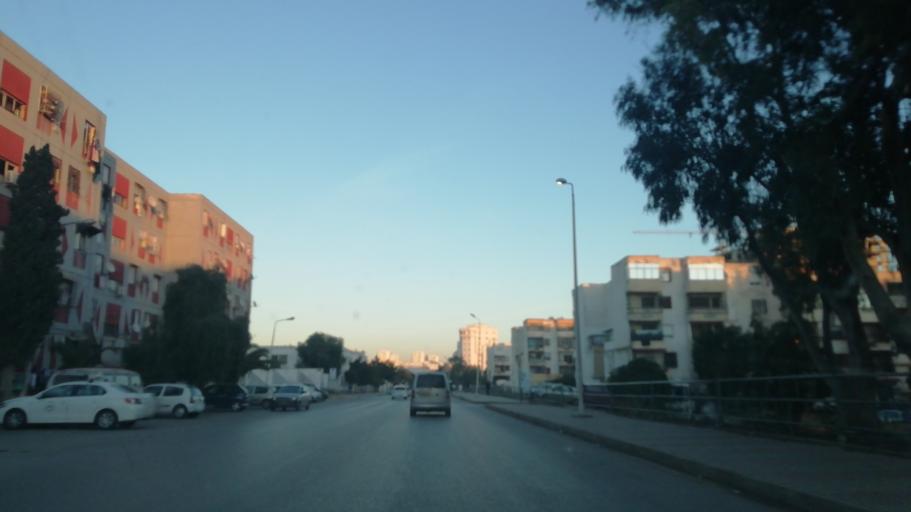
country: DZ
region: Oran
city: Oran
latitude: 35.6983
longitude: -0.5938
